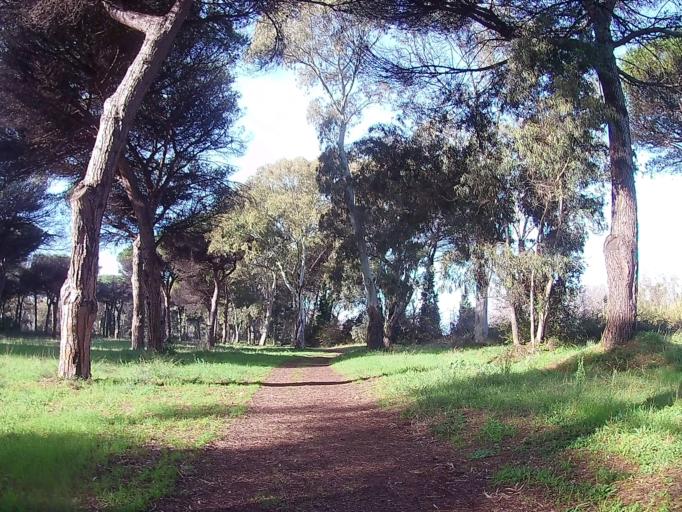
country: IT
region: Latium
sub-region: Citta metropolitana di Roma Capitale
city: Lido di Ostia
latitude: 41.7462
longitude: 12.2787
